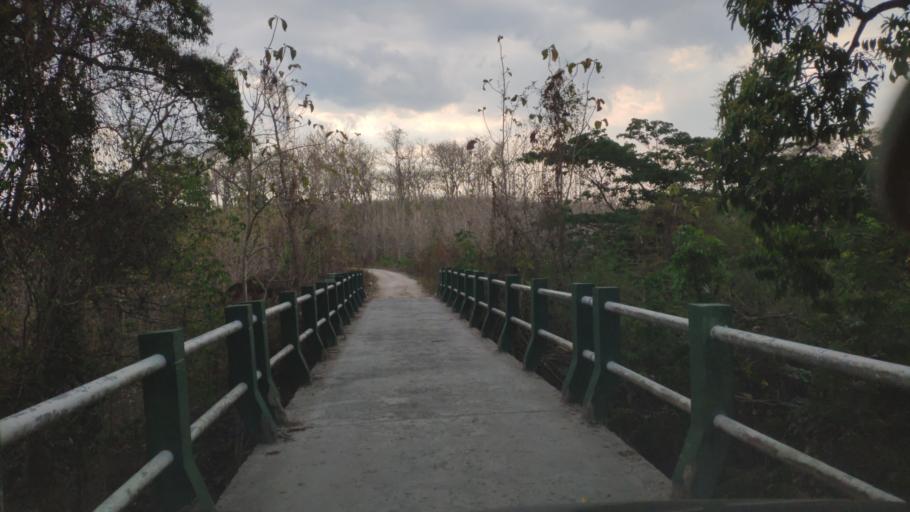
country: ID
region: Central Java
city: Randublatung
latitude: -7.2872
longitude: 111.3006
